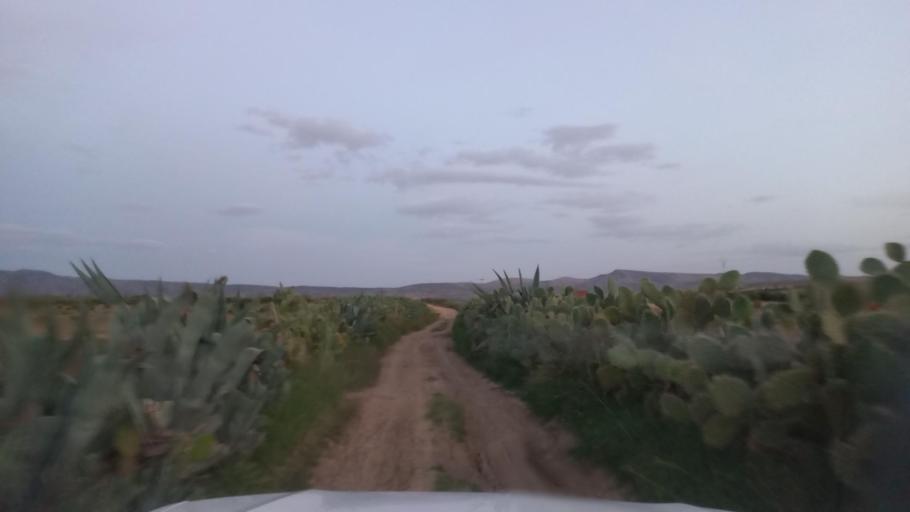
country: TN
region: Al Qasrayn
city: Sbiba
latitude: 35.4213
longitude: 9.1127
